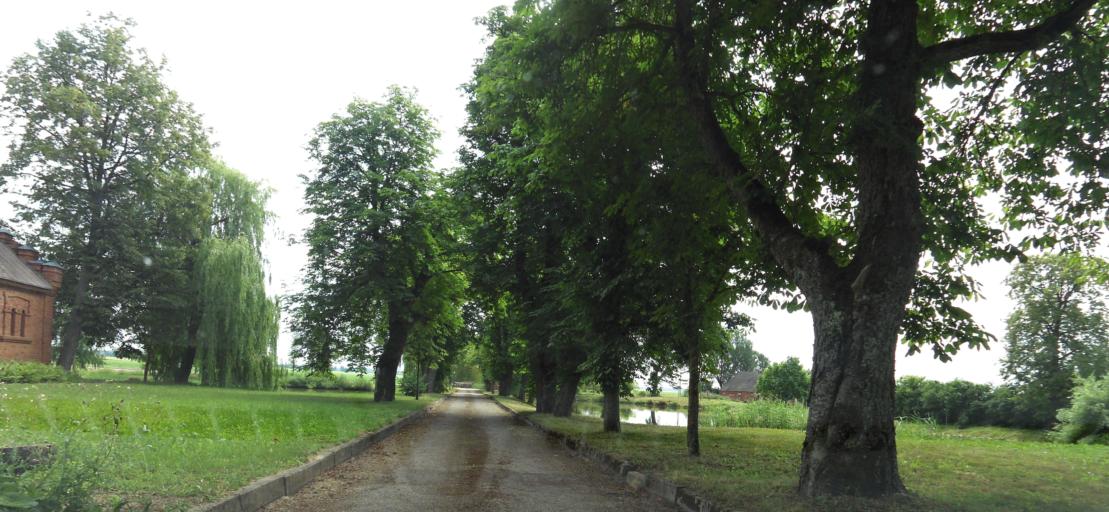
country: LT
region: Panevezys
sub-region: Birzai
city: Birzai
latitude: 56.2888
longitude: 24.6053
